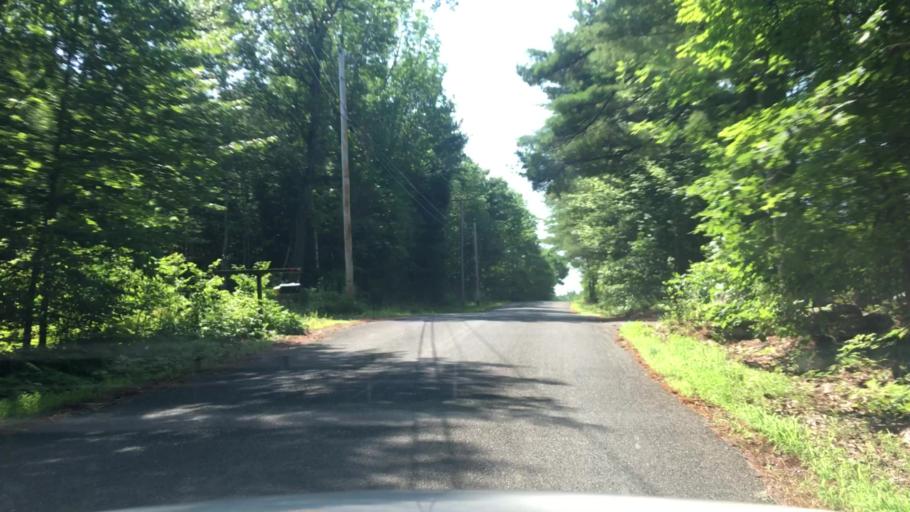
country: US
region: Maine
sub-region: Androscoggin County
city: Greene
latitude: 44.2267
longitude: -70.1053
